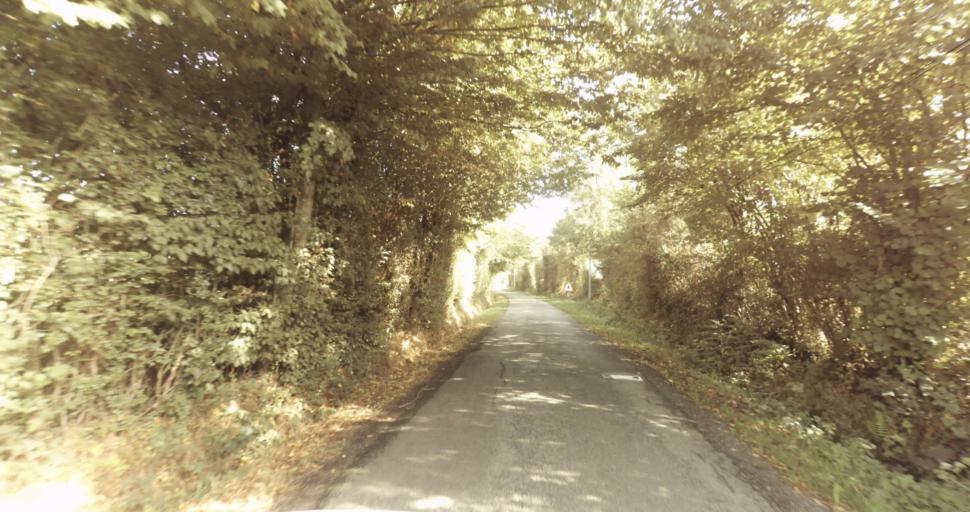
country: FR
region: Lower Normandy
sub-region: Departement de l'Orne
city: Gace
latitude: 48.8705
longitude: 0.3302
